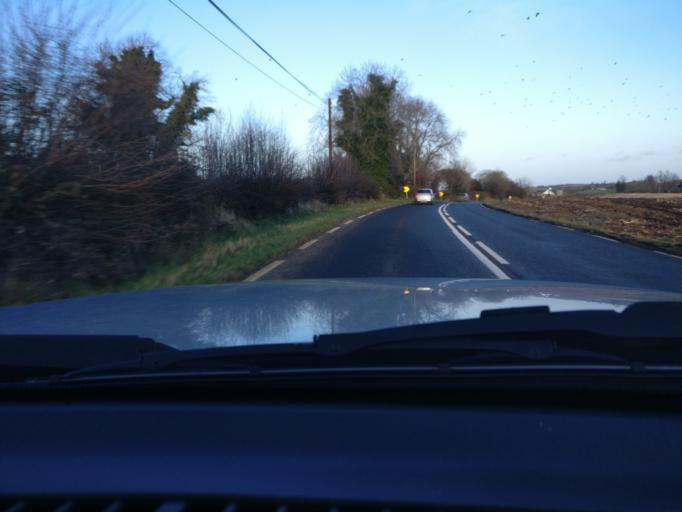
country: IE
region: Leinster
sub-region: Lu
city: Ardee
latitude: 53.8473
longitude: -6.5994
